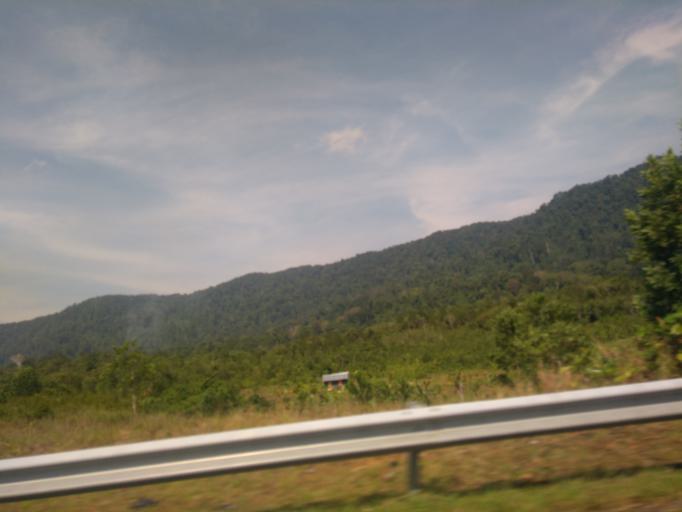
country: MY
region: Sarawak
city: Kuching
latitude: 1.6397
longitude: 110.1953
